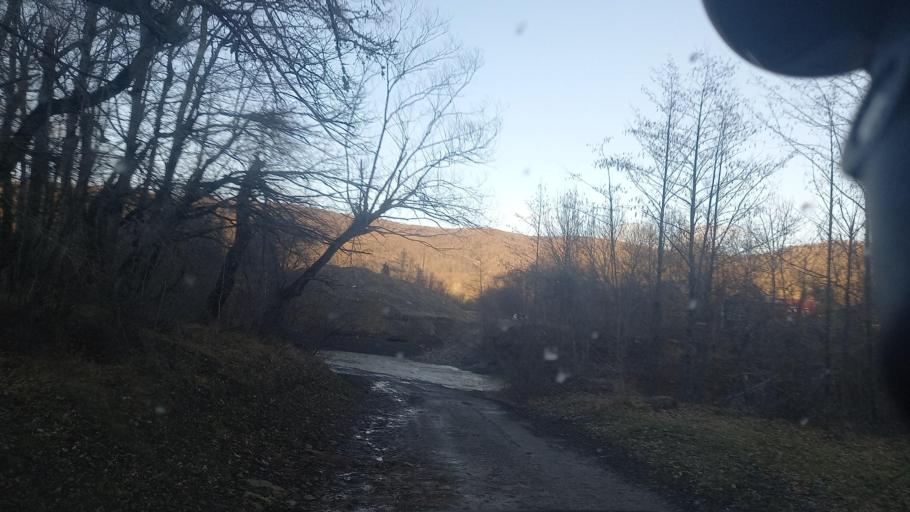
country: RU
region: Krasnodarskiy
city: Smolenskaya
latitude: 44.6143
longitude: 38.7431
